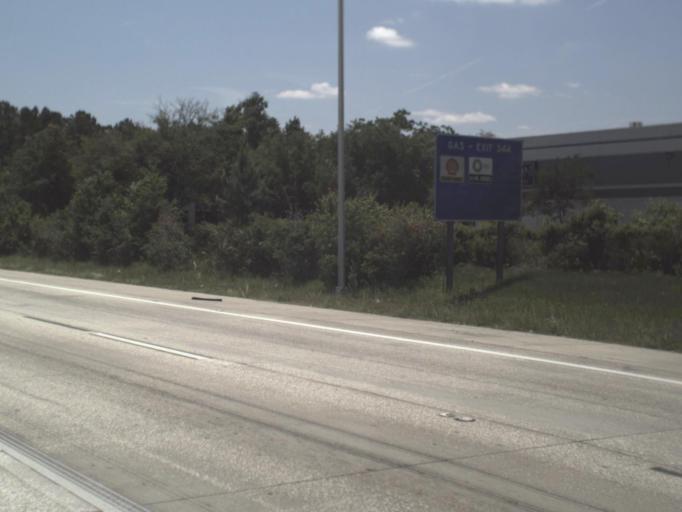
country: US
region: Florida
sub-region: Duval County
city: Jacksonville
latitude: 30.2535
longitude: -81.5989
